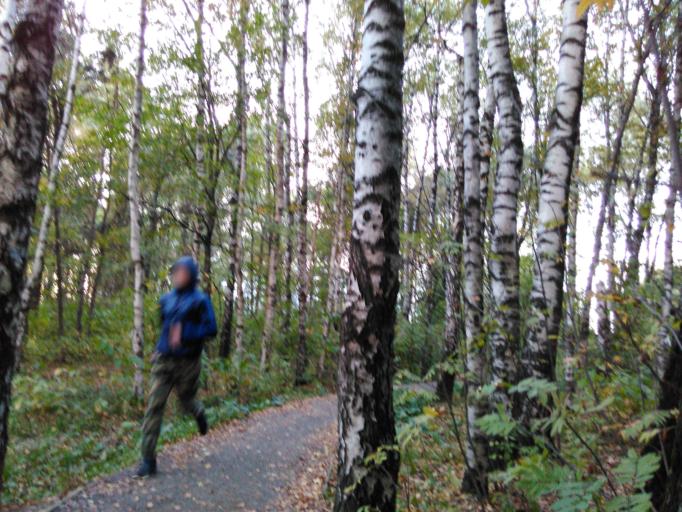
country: RU
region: Moscow
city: Troparevo
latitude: 55.6517
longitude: 37.5108
